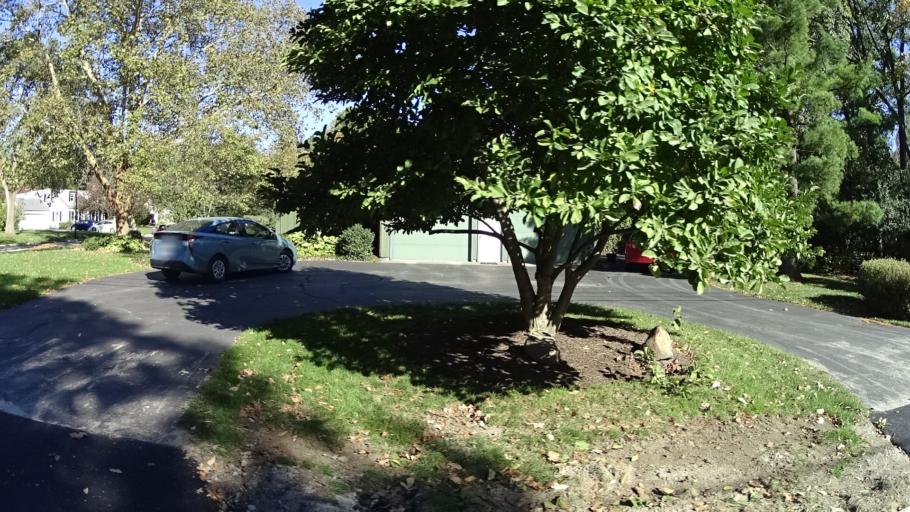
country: US
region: Ohio
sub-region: Lorain County
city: Oberlin
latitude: 41.2871
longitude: -82.2337
